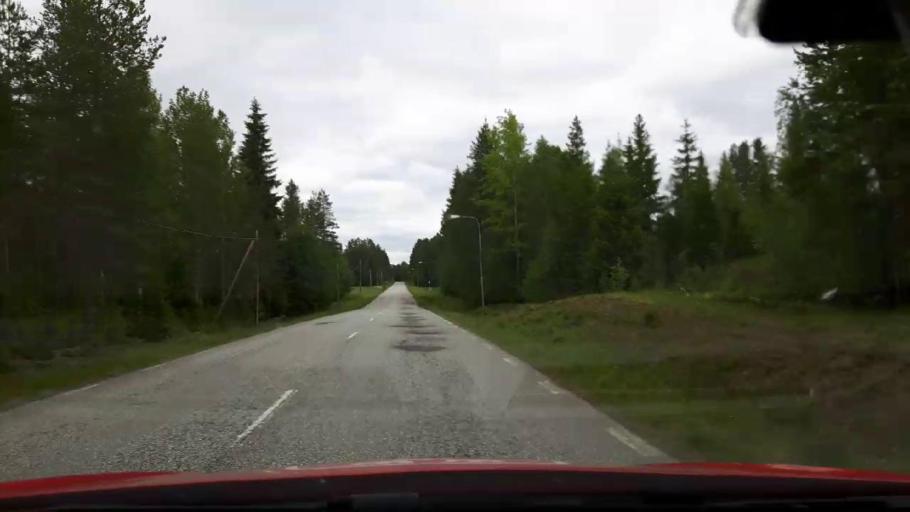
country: SE
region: Jaemtland
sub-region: Ragunda Kommun
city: Hammarstrand
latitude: 63.2250
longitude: 15.9311
